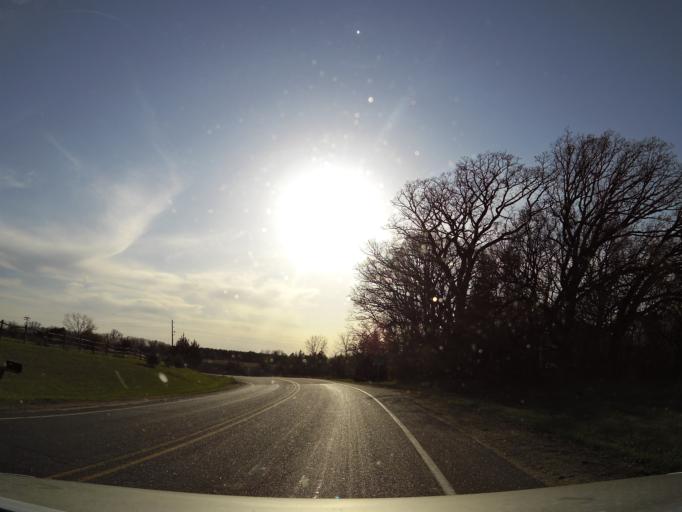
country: US
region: Minnesota
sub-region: Washington County
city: Afton
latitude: 44.8259
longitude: -92.7316
